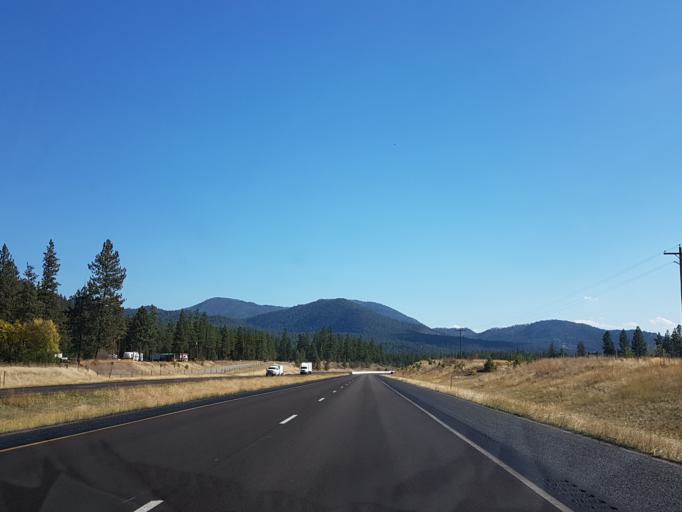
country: US
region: Montana
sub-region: Mineral County
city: Superior
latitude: 47.1364
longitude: -114.8030
